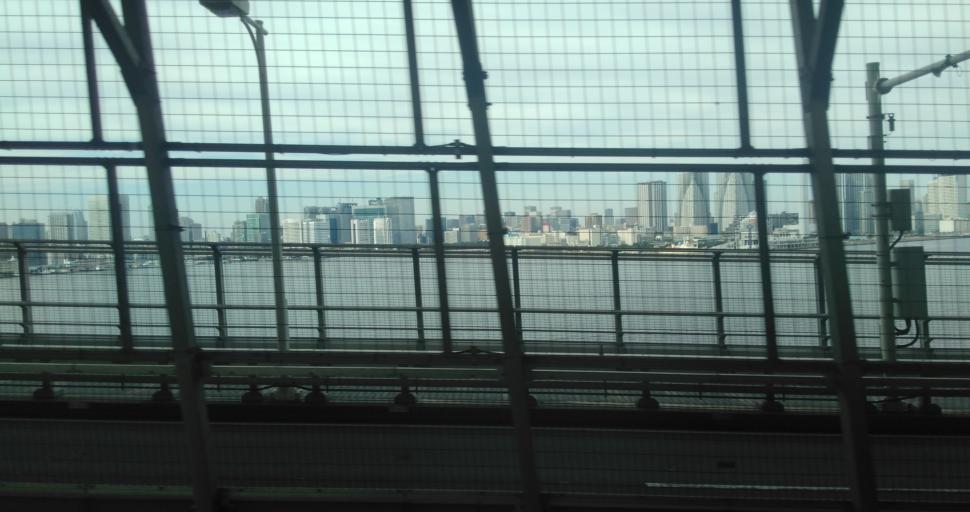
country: JP
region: Tokyo
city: Tokyo
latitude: 35.6354
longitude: 139.7715
